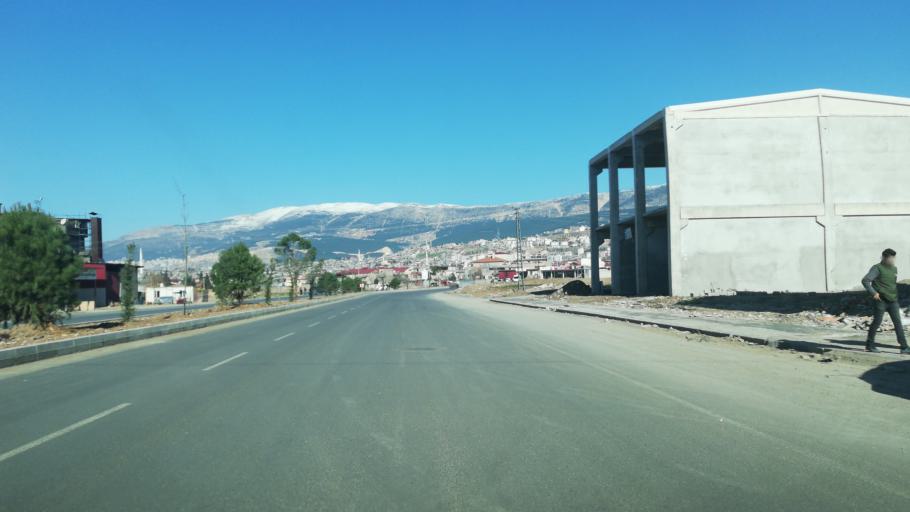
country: TR
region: Kahramanmaras
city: Kahramanmaras
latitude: 37.5681
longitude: 36.9645
